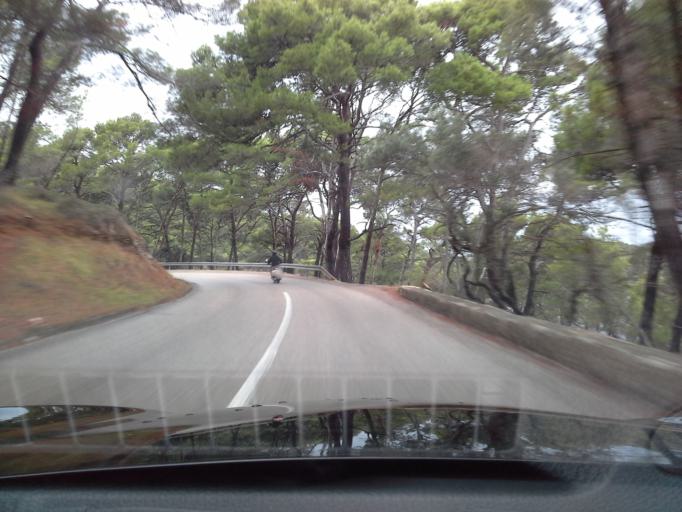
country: HR
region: Primorsko-Goranska
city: Mali Losinj
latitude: 44.5248
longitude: 14.4934
